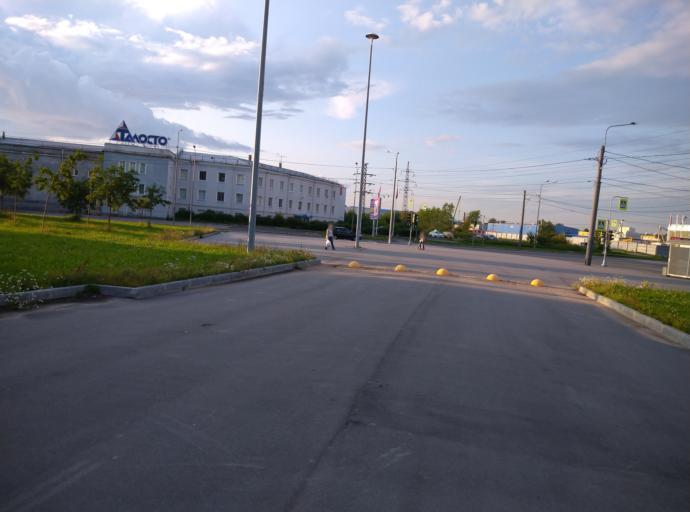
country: RU
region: St.-Petersburg
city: Kupchino
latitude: 59.8714
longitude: 30.3436
